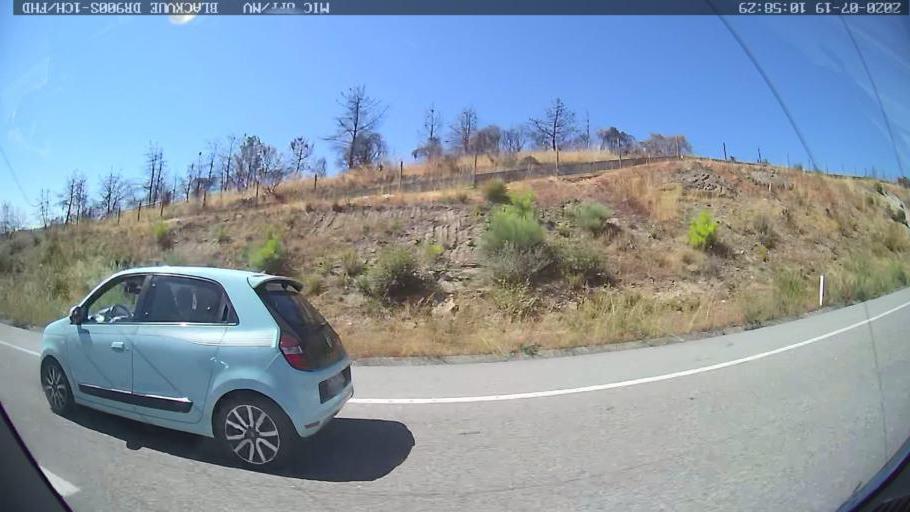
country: PT
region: Vila Real
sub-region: Murca
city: Murca
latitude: 41.3891
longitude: -7.4706
